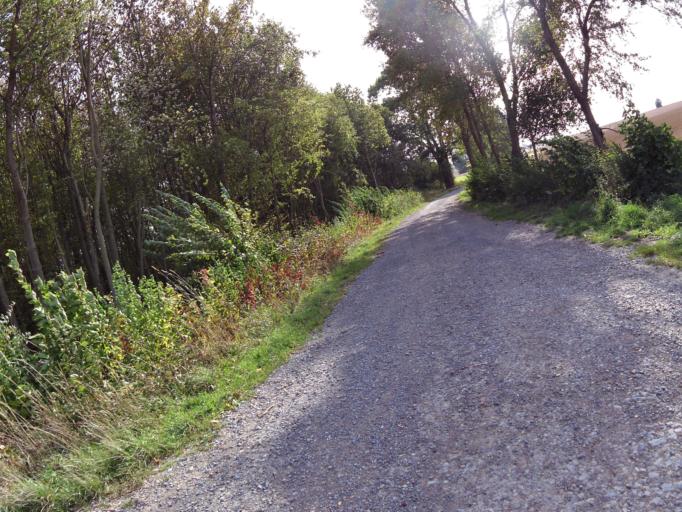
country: DE
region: Bavaria
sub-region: Regierungsbezirk Unterfranken
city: Reichenberg
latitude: 49.7041
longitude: 9.9511
